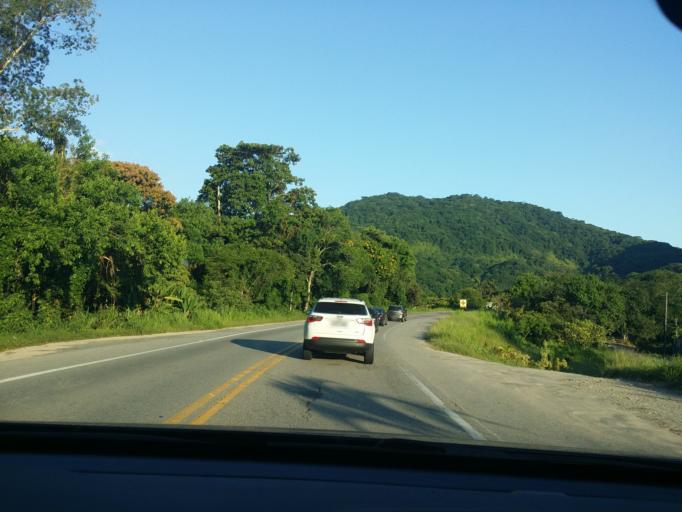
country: BR
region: Sao Paulo
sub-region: Sao Sebastiao
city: Sao Sebastiao
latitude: -23.7687
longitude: -45.6413
